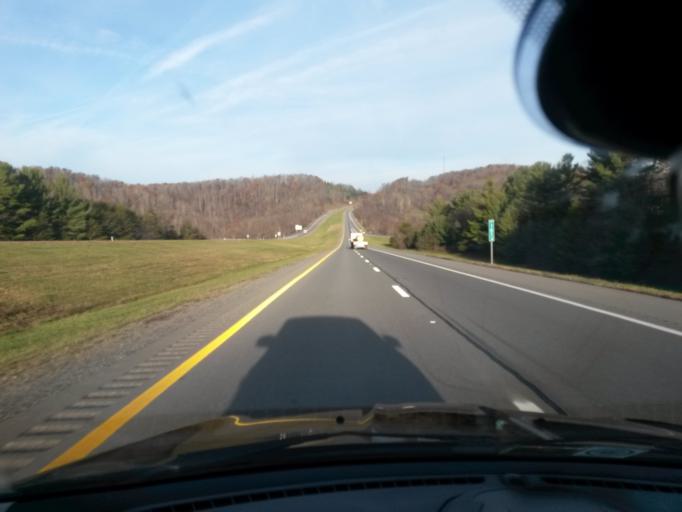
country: US
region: West Virginia
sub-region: Greenbrier County
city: Lewisburg
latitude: 37.8687
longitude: -80.5544
